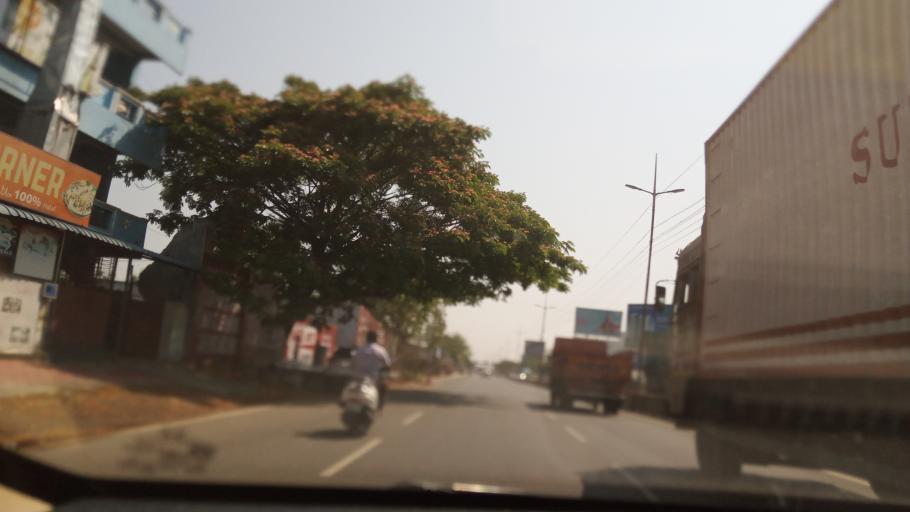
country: IN
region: Tamil Nadu
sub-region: Coimbatore
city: Irugur
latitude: 11.0590
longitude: 77.0808
